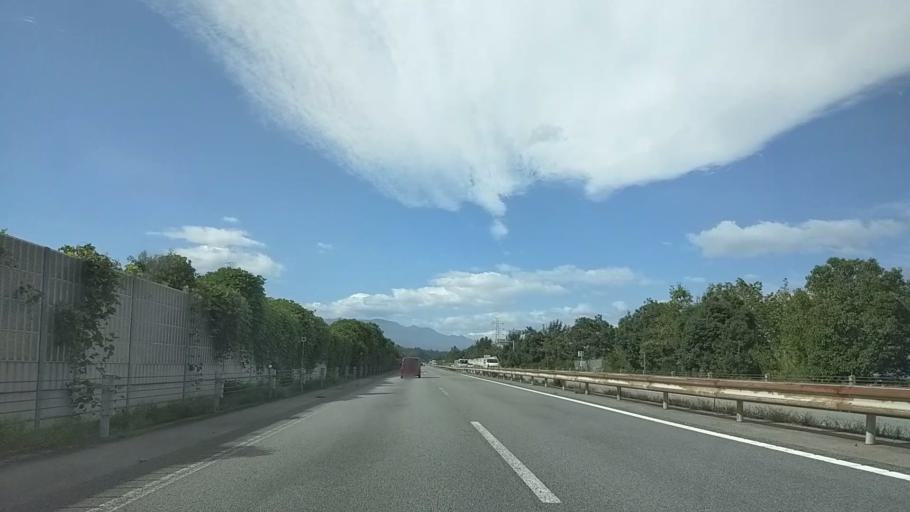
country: JP
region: Yamanashi
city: Isawa
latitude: 35.6103
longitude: 138.6186
